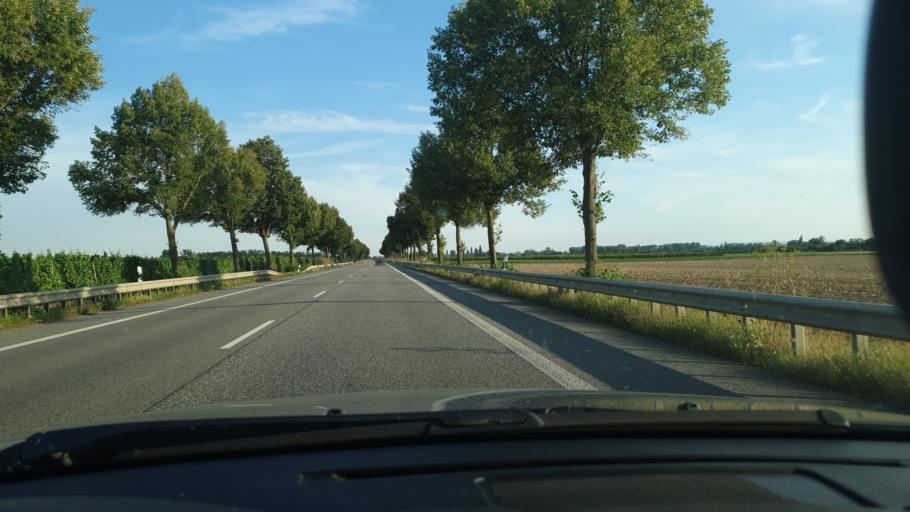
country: DE
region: Rheinland-Pfalz
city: Alsheim
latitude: 49.7488
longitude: 8.3520
